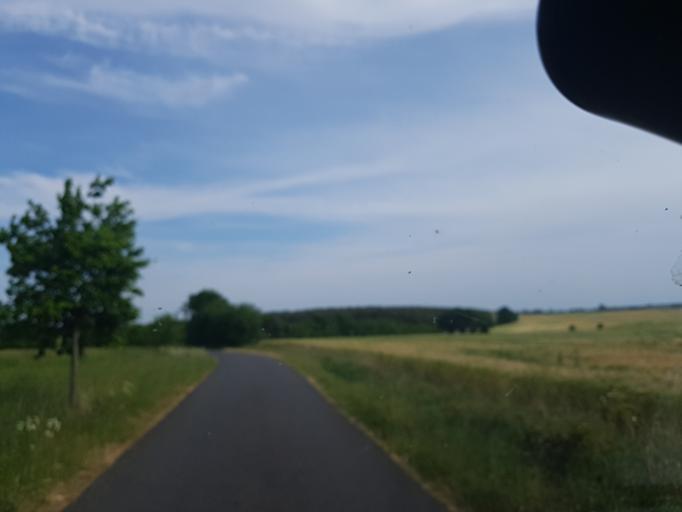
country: DE
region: Brandenburg
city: Niemegk
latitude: 52.0036
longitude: 12.6699
